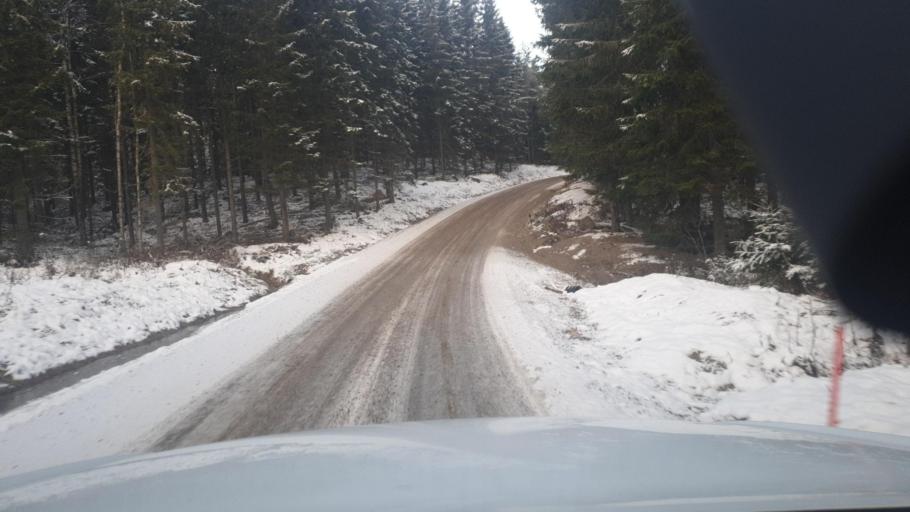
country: SE
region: Vaermland
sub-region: Arvika Kommun
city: Arvika
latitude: 59.9617
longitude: 12.6579
